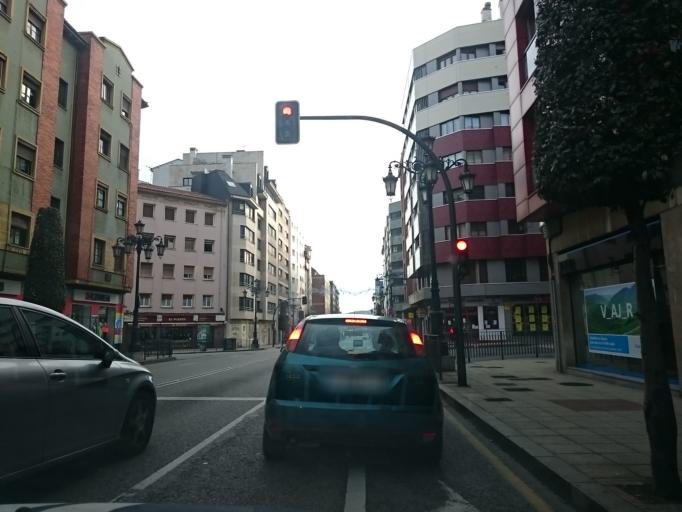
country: ES
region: Asturias
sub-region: Province of Asturias
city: Oviedo
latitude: 43.3609
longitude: -5.8388
